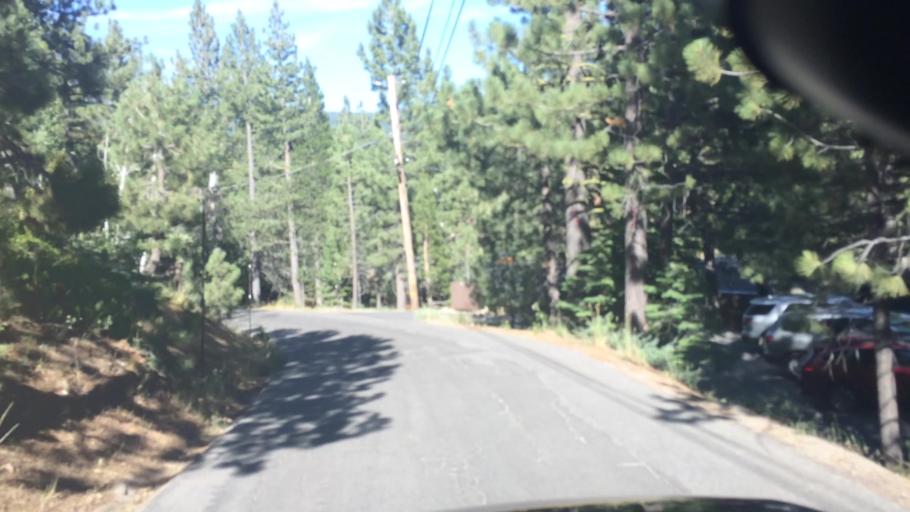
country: US
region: California
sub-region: Placer County
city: Sunnyside-Tahoe City
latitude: 39.1994
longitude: -120.2316
